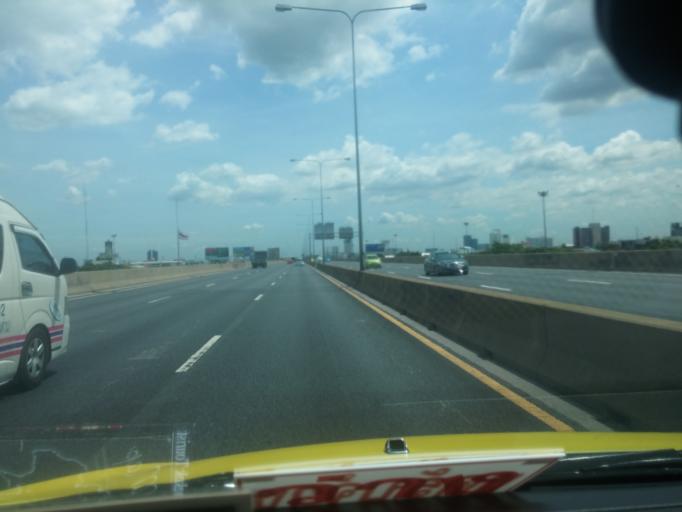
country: TH
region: Bangkok
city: Chatuchak
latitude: 13.8290
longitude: 100.5576
